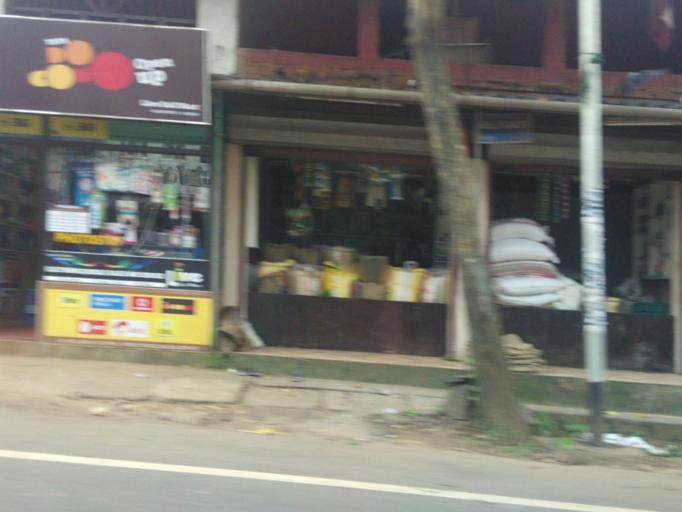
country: IN
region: Kerala
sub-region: Kozhikode
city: Kunnamangalam
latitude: 11.3021
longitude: 75.8628
